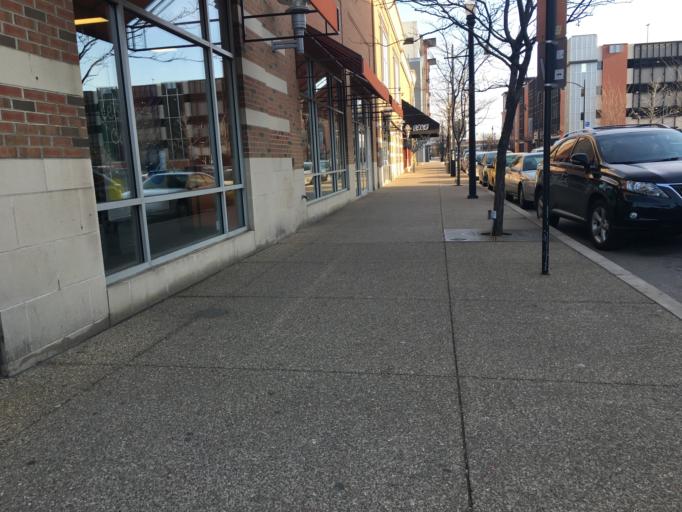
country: US
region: Pennsylvania
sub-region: Allegheny County
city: Mount Oliver
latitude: 40.4276
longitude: -79.9655
